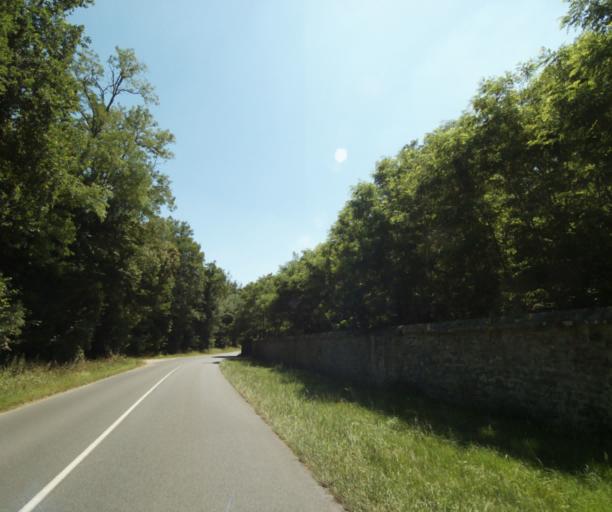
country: FR
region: Ile-de-France
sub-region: Departement de Seine-et-Marne
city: Noisy-sur-Ecole
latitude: 48.3813
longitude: 2.4988
